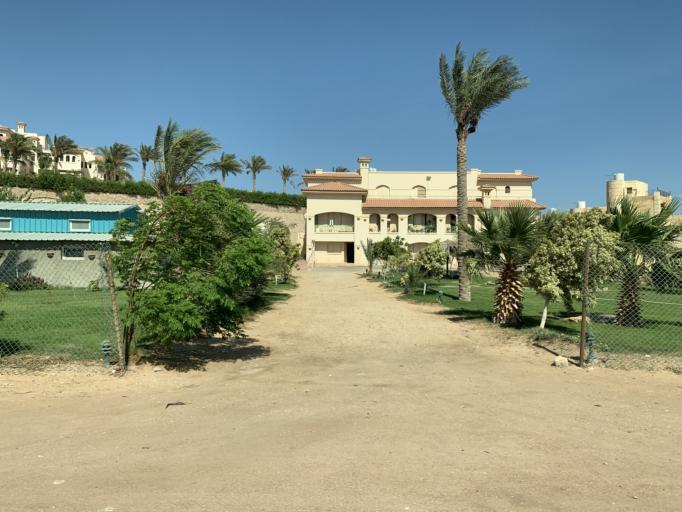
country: EG
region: As Suways
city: Ain Sukhna
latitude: 29.2211
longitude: 32.6208
